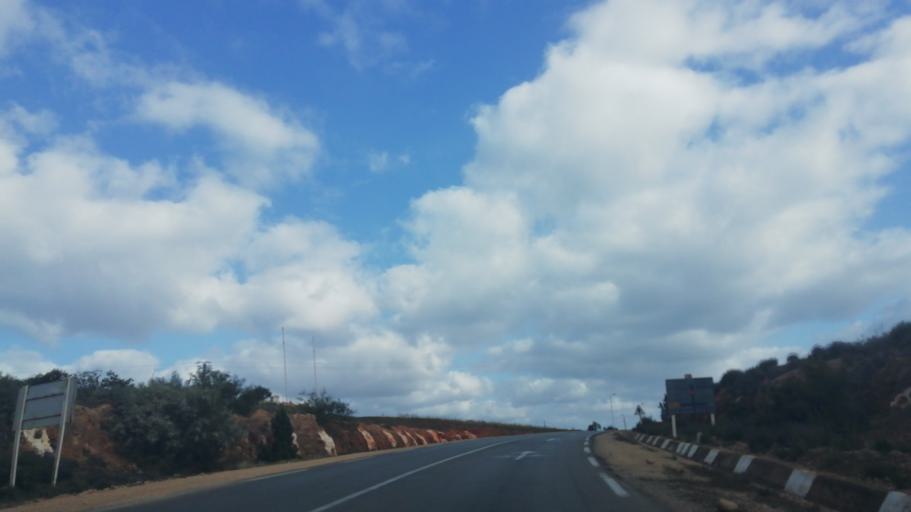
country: DZ
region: Relizane
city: Mazouna
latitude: 36.2437
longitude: 0.5366
